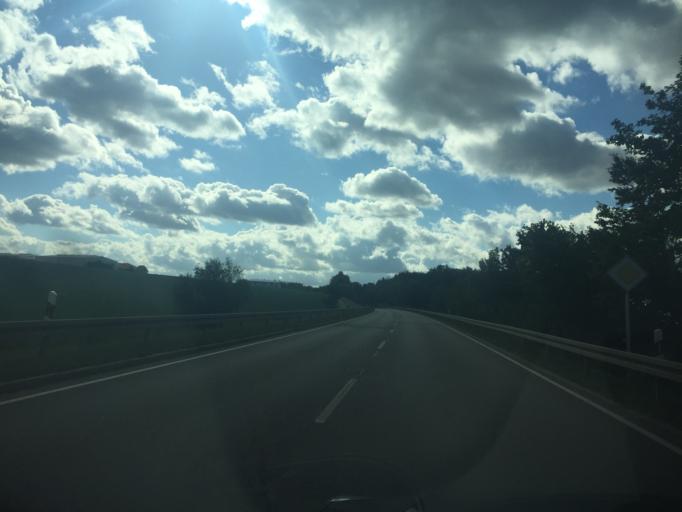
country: DE
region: Bavaria
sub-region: Upper Palatinate
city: Poppenricht
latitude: 49.4967
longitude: 11.8268
